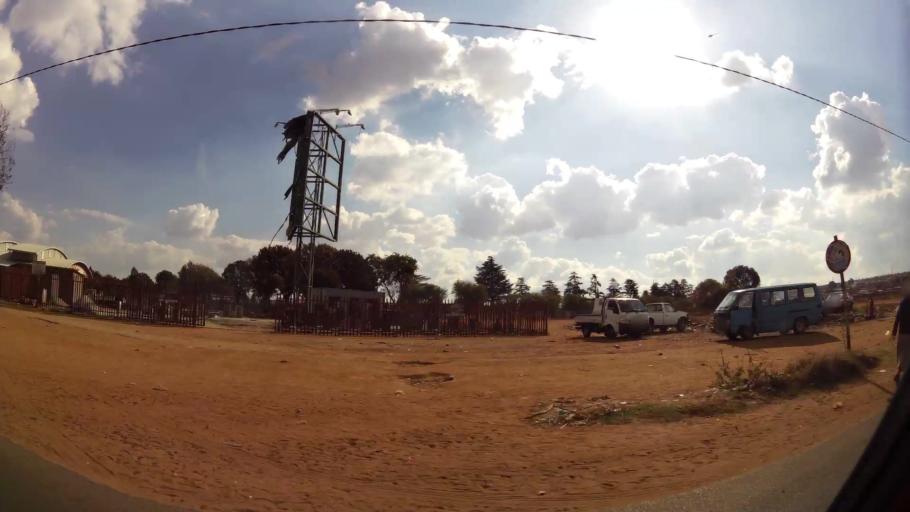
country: ZA
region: Gauteng
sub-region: City of Johannesburg Metropolitan Municipality
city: Roodepoort
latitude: -26.2088
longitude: 27.8707
